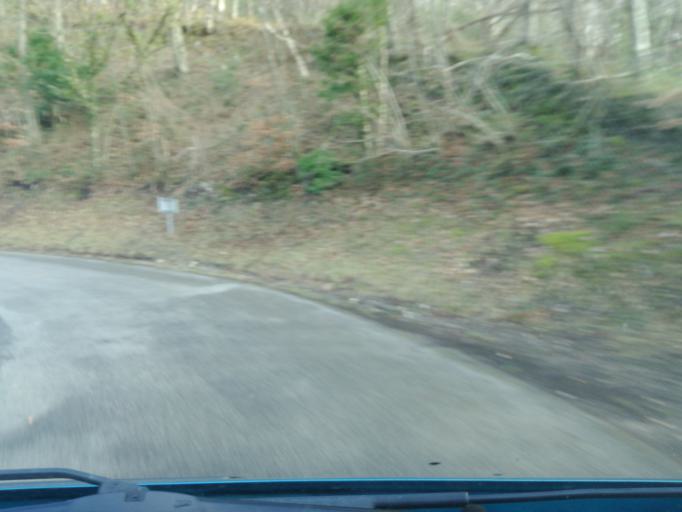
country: FR
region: Haute-Normandie
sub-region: Departement de la Seine-Maritime
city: Yport
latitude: 49.7323
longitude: 0.3244
